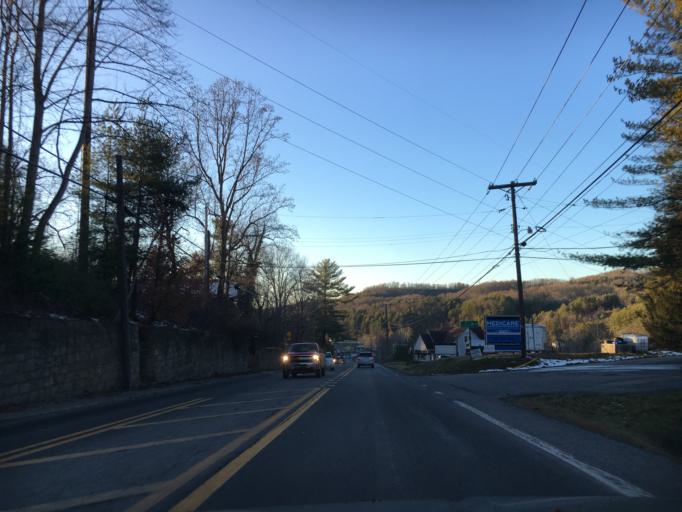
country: US
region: West Virginia
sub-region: Raleigh County
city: Daniels
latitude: 37.7466
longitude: -81.1274
